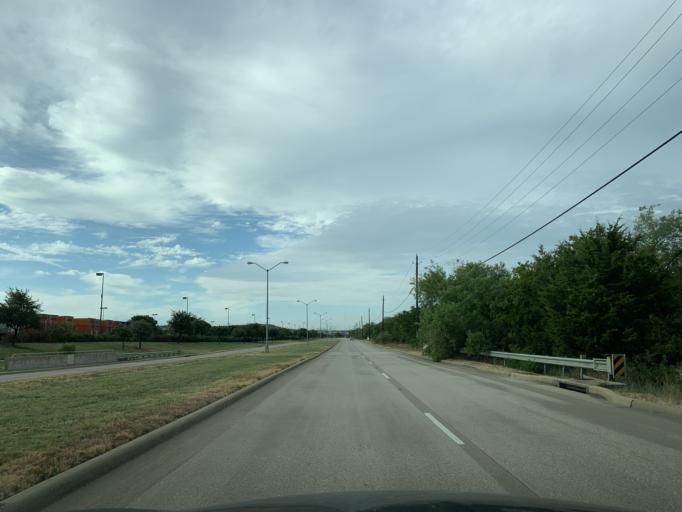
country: US
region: Texas
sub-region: Dallas County
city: Grand Prairie
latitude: 32.6951
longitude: -96.9633
